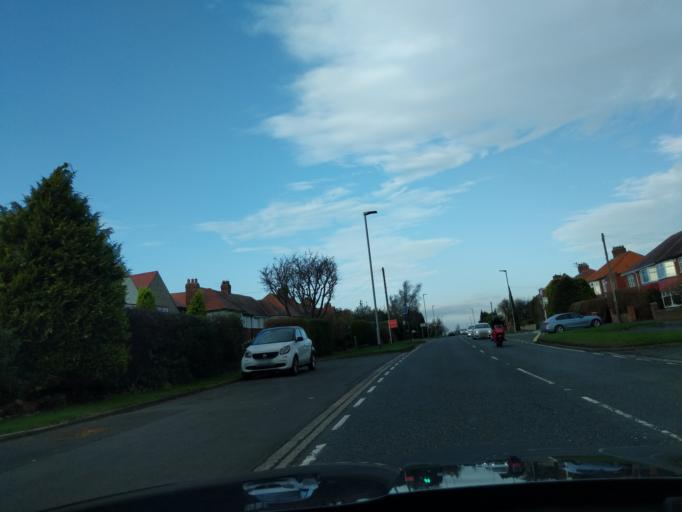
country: GB
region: England
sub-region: Northumberland
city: Ponteland
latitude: 55.0456
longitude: -1.7298
